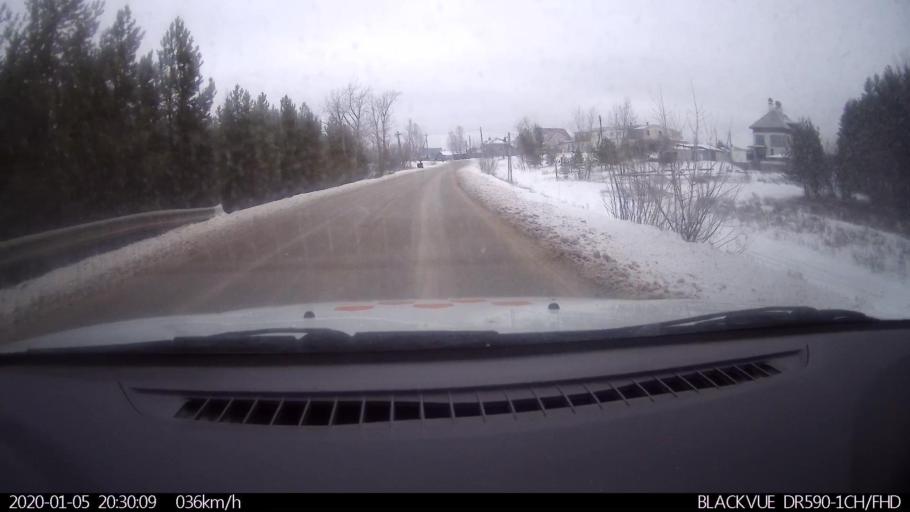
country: RU
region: Nizjnij Novgorod
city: Lukino
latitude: 56.3966
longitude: 43.7293
